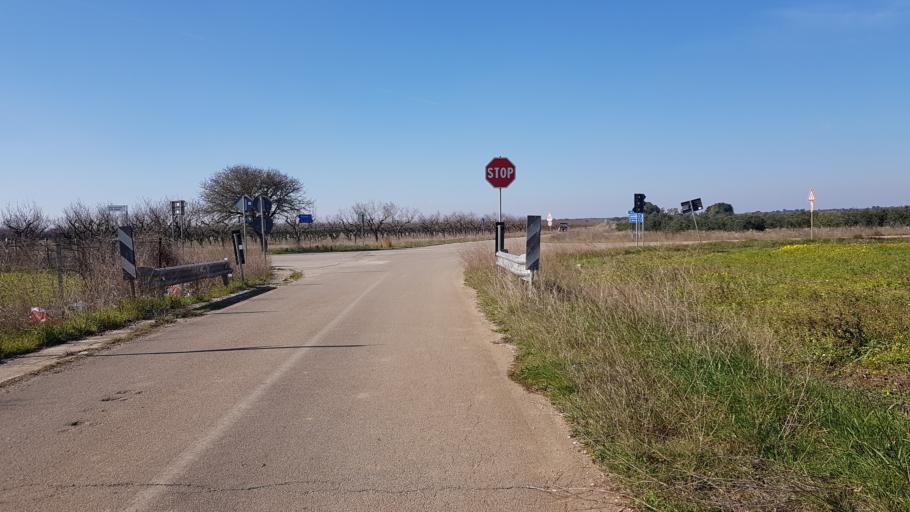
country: IT
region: Apulia
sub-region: Provincia di Brindisi
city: Mesagne
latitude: 40.6198
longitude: 17.7851
